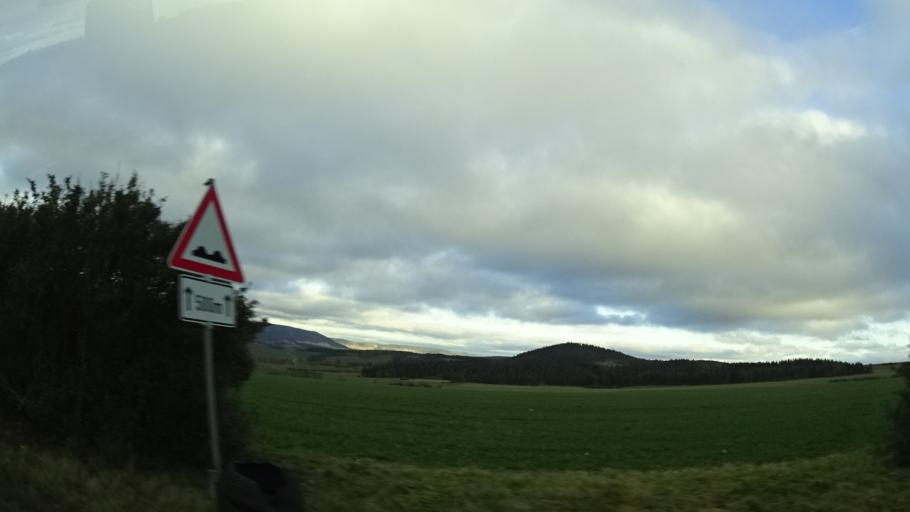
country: DE
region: Thuringia
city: Rottenbach
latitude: 50.7371
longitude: 11.2138
